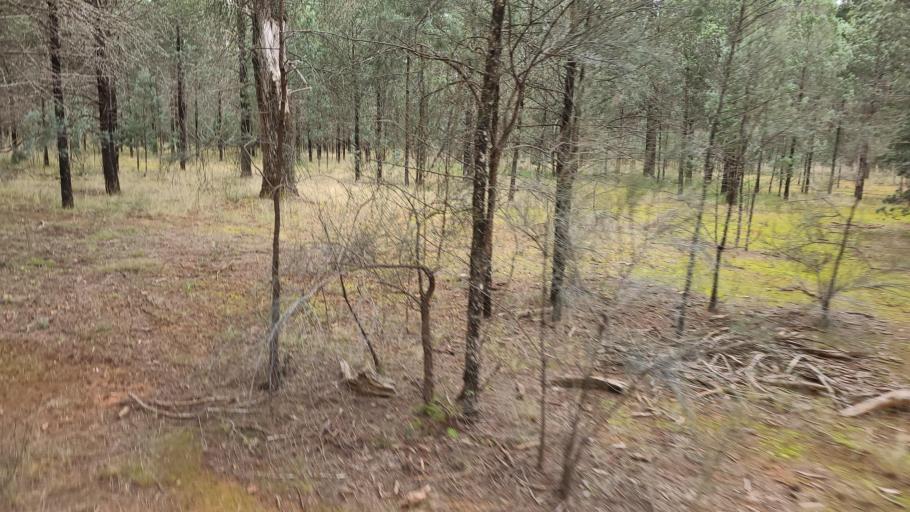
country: AU
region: New South Wales
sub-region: Coolamon
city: Coolamon
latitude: -34.8588
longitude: 146.9213
